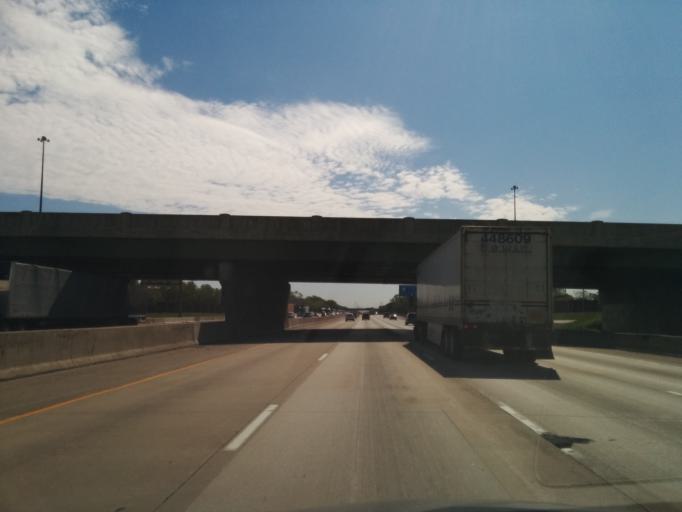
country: US
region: Indiana
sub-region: Lake County
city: Munster
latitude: 41.5740
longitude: -87.5097
